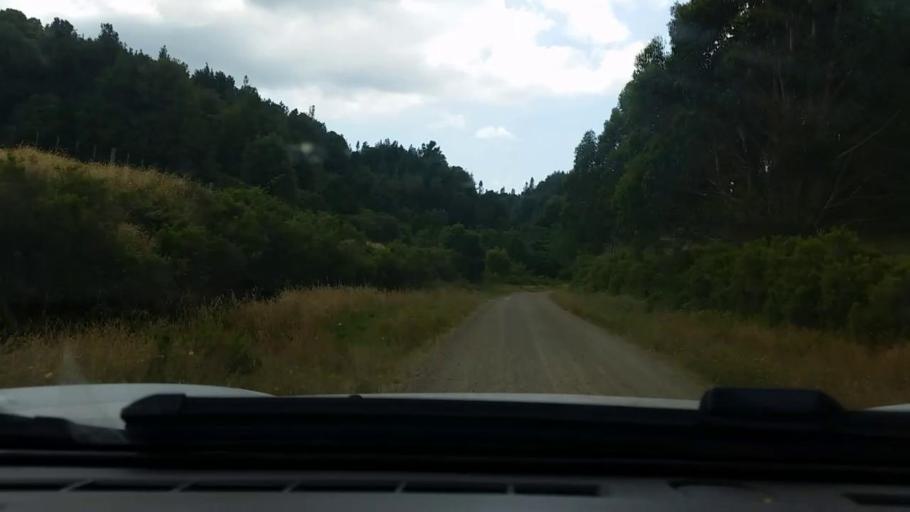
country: NZ
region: Bay of Plenty
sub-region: Kawerau District
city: Kawerau
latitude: -38.0104
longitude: 176.5974
